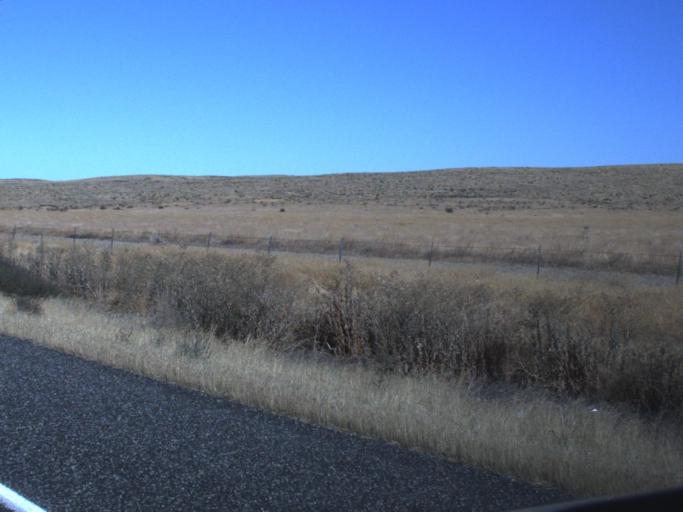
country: US
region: Washington
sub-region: Benton County
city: Benton City
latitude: 46.4886
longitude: -119.5873
